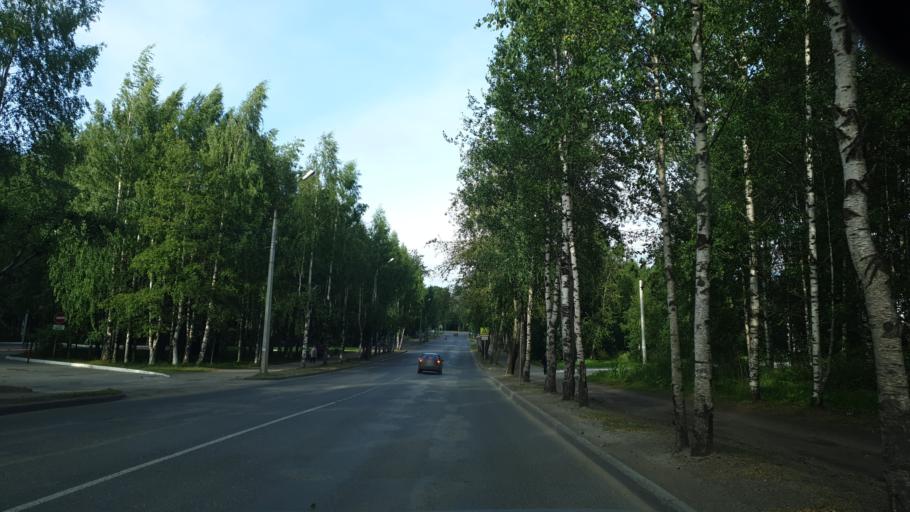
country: RU
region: Komi Republic
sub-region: Syktyvdinskiy Rayon
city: Syktyvkar
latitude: 61.6589
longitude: 50.8134
